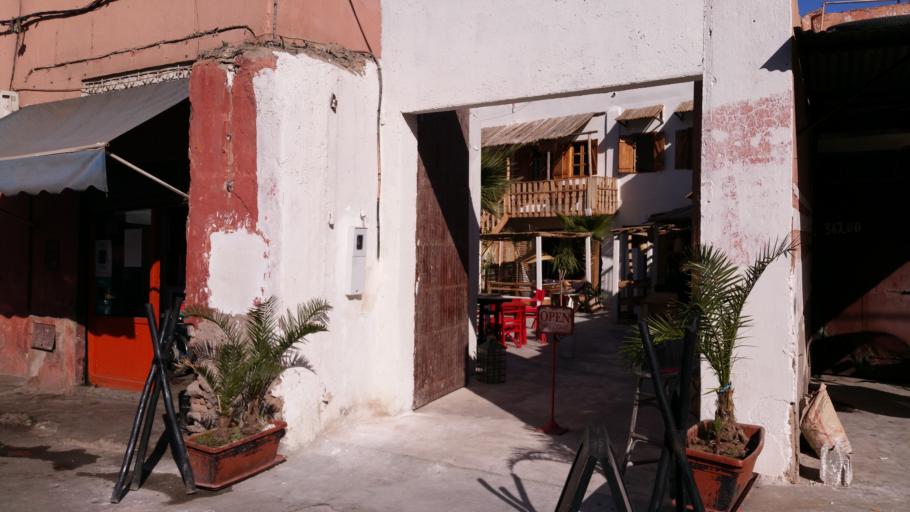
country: MA
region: Marrakech-Tensift-Al Haouz
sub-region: Marrakech
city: Marrakesh
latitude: 31.6342
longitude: -7.9908
